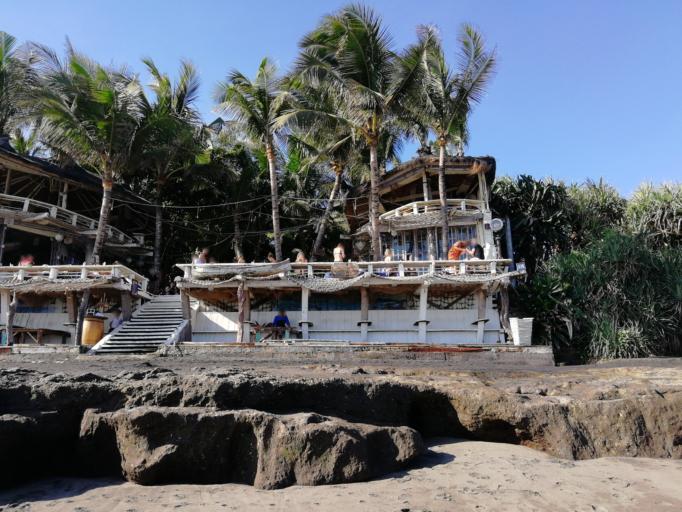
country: ID
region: Bali
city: Banjar Kerobokan
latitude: -8.6548
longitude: 115.1247
